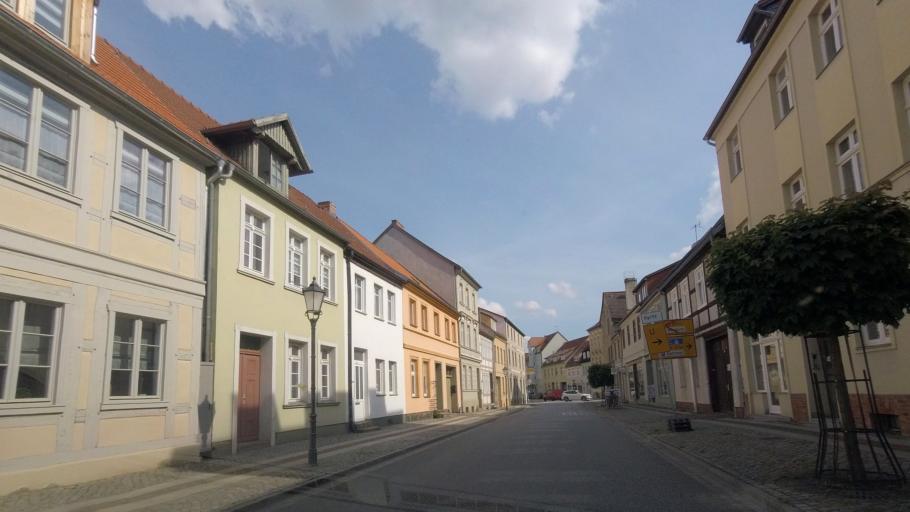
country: DE
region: Brandenburg
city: Wittstock
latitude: 53.1631
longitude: 12.4822
